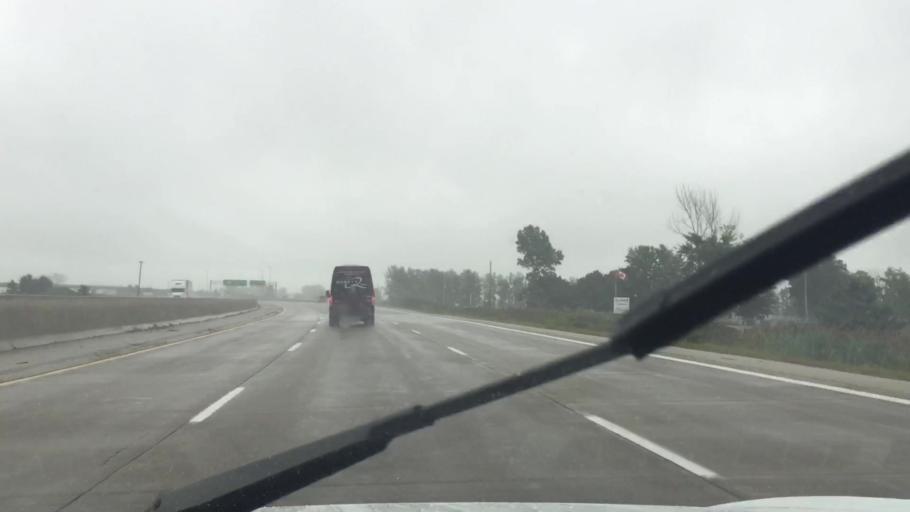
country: CA
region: Ontario
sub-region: Lambton County
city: Walpole Island
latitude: 42.2595
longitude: -82.4642
